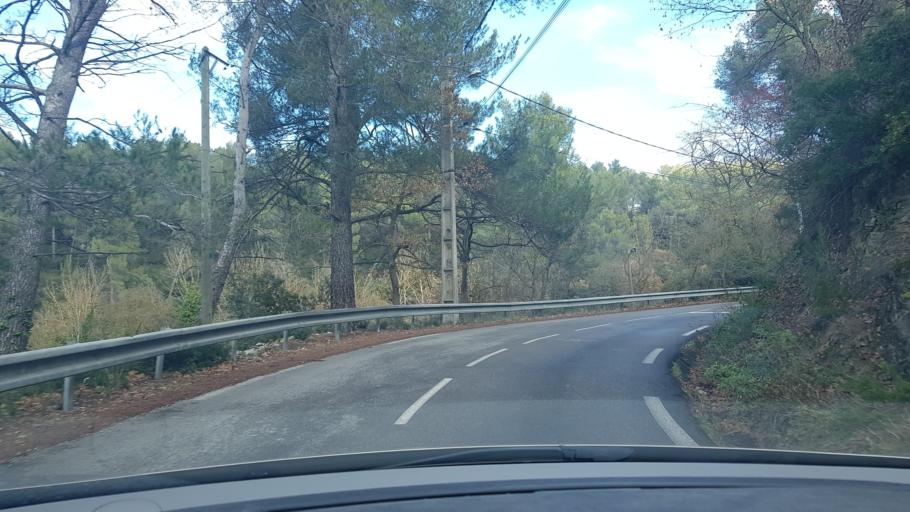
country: FR
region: Provence-Alpes-Cote d'Azur
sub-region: Departement des Bouches-du-Rhone
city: Simiane-Collongue
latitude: 43.4247
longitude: 5.4490
